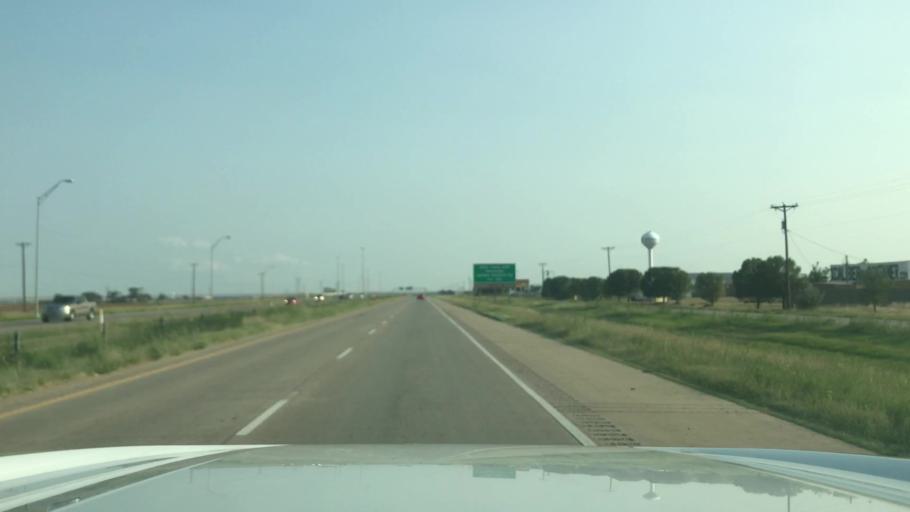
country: US
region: Texas
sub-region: Randall County
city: Canyon
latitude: 35.0342
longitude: -101.9194
